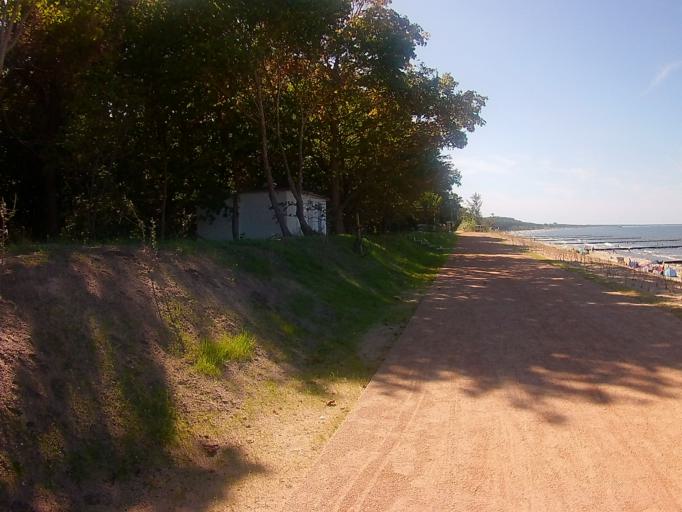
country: DE
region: Mecklenburg-Vorpommern
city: Ostseebad Zinnowitz
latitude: 54.0720
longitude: 13.9488
